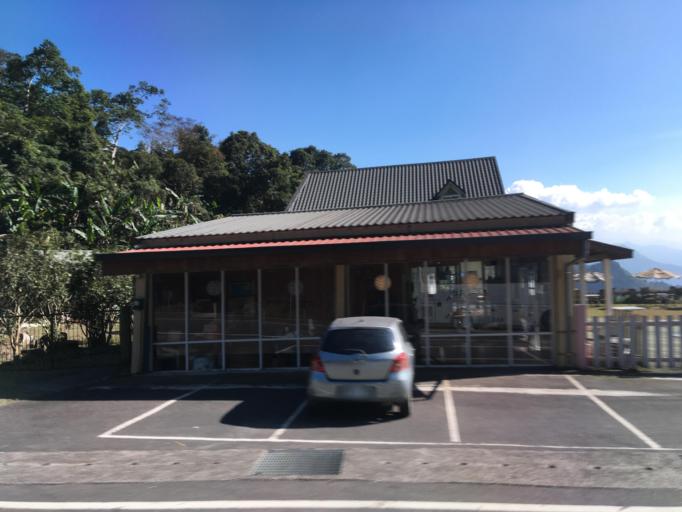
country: TW
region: Taiwan
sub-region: Chiayi
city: Jiayi Shi
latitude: 23.4390
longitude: 120.6662
